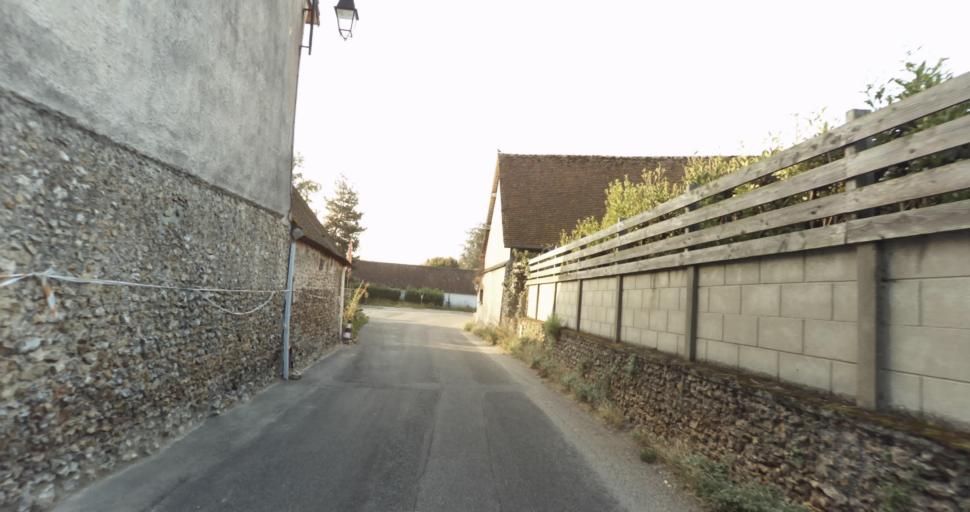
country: FR
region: Haute-Normandie
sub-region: Departement de l'Eure
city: Marcilly-sur-Eure
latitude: 48.7851
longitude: 1.3445
